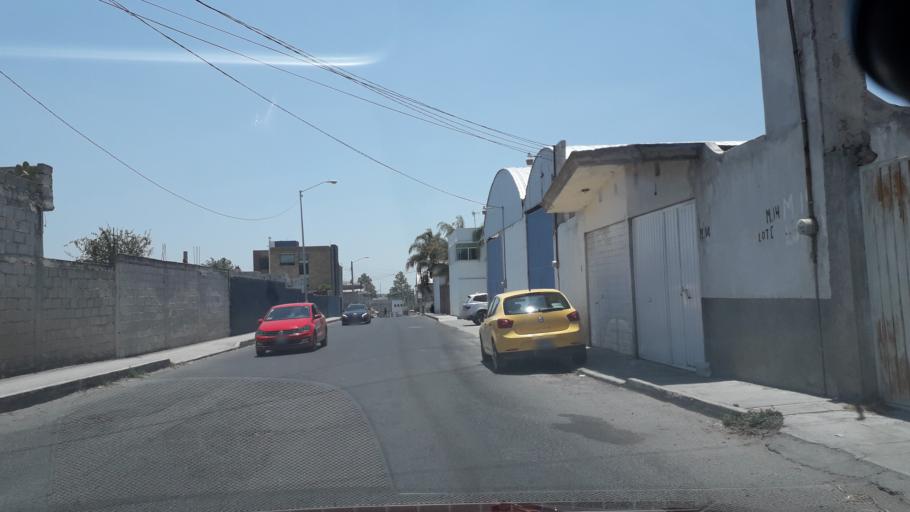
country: MX
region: Puebla
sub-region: Puebla
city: Articulo Primero Constitucional
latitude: 18.9920
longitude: -98.1836
